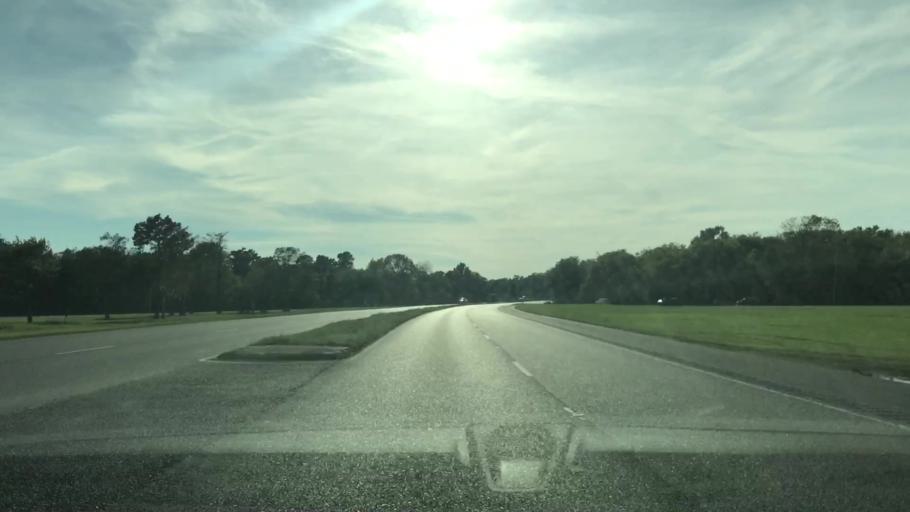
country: US
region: Louisiana
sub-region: Jefferson Parish
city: Bridge City
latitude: 29.9125
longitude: -90.1775
